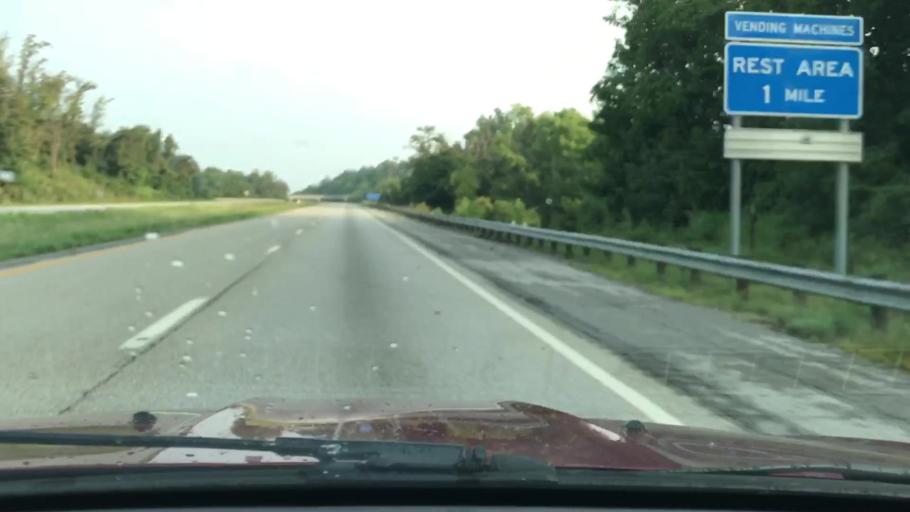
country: US
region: Ohio
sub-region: Washington County
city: Marietta
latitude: 39.4371
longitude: -81.4304
